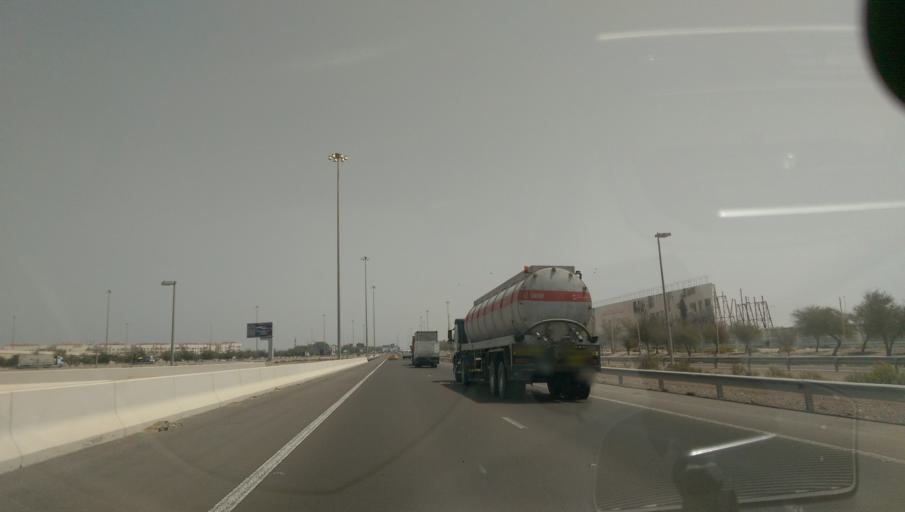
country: AE
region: Abu Dhabi
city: Abu Dhabi
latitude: 24.5440
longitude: 54.6939
